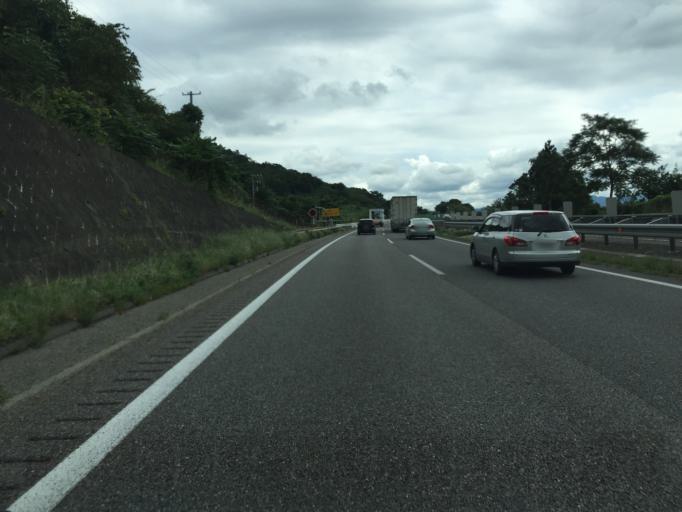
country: JP
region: Fukushima
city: Yanagawamachi-saiwaicho
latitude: 37.8922
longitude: 140.5585
